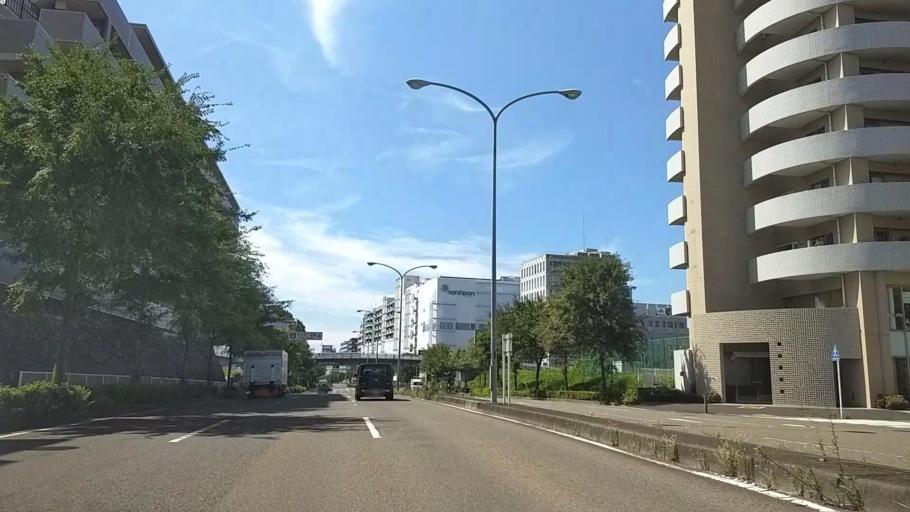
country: JP
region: Tokyo
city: Chofugaoka
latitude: 35.5546
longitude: 139.5817
